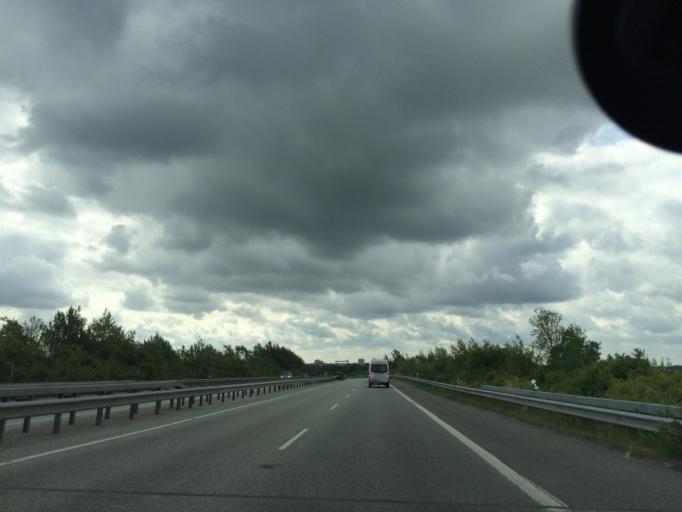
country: DE
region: Schleswig-Holstein
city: Ottendorf
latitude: 54.3670
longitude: 10.0791
